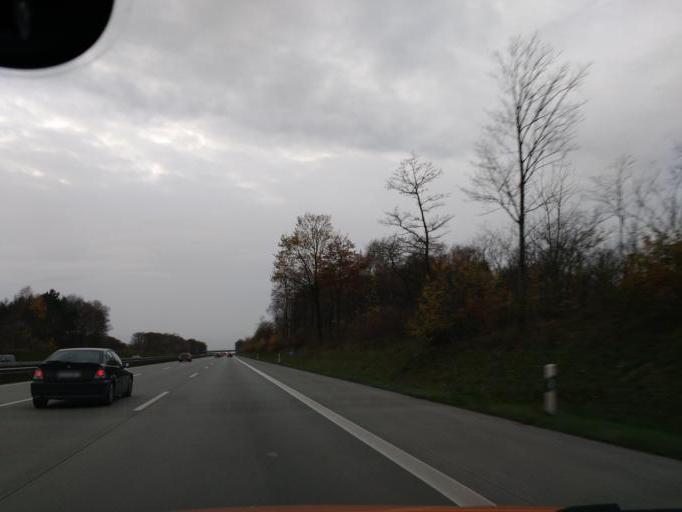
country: DE
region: Lower Saxony
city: Ottersberg
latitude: 53.0731
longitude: 9.1348
